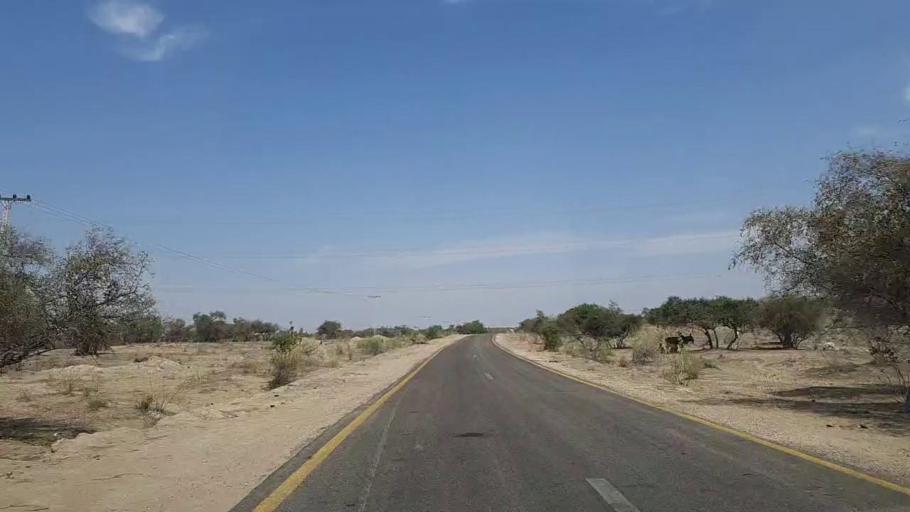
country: PK
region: Sindh
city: Mithi
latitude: 24.8509
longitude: 69.8378
